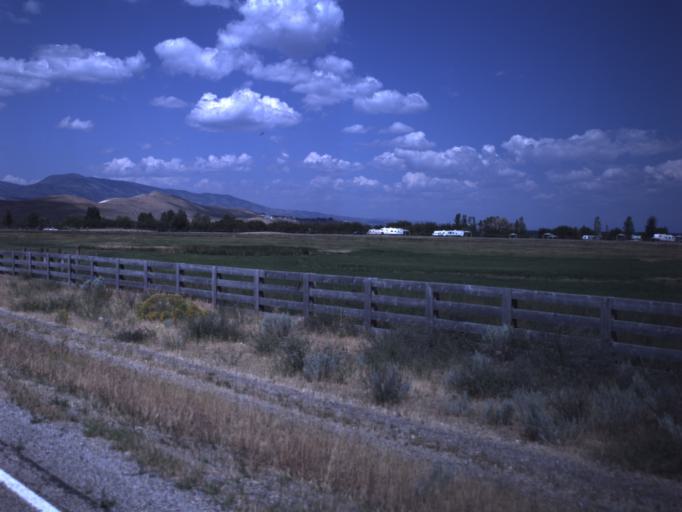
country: US
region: Utah
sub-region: Rich County
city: Randolph
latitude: 41.8419
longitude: -111.3456
